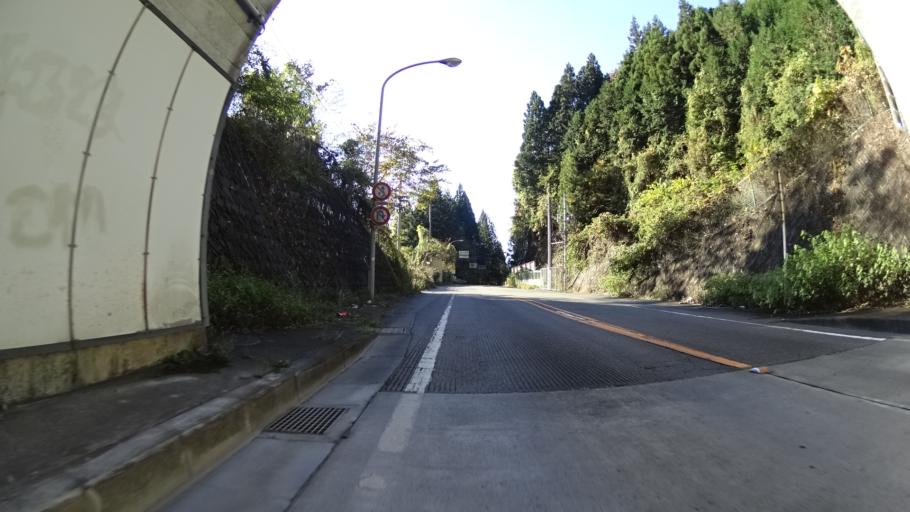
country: JP
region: Yamanashi
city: Uenohara
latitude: 35.6911
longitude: 139.1039
